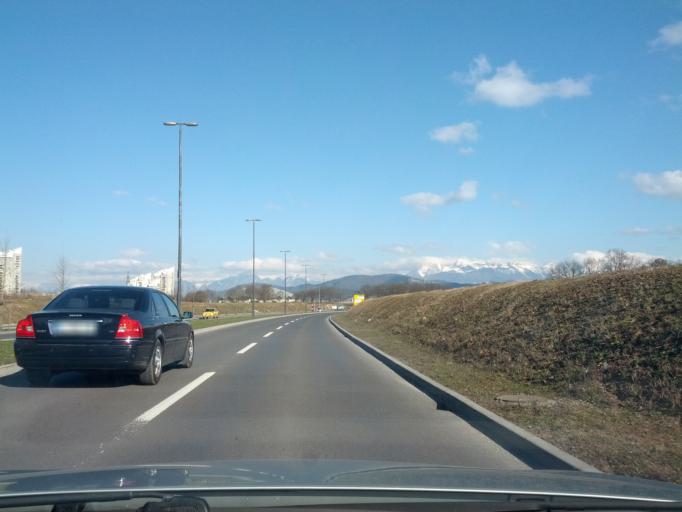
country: SI
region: Ljubljana
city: Ljubljana
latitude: 46.0721
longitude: 14.5252
